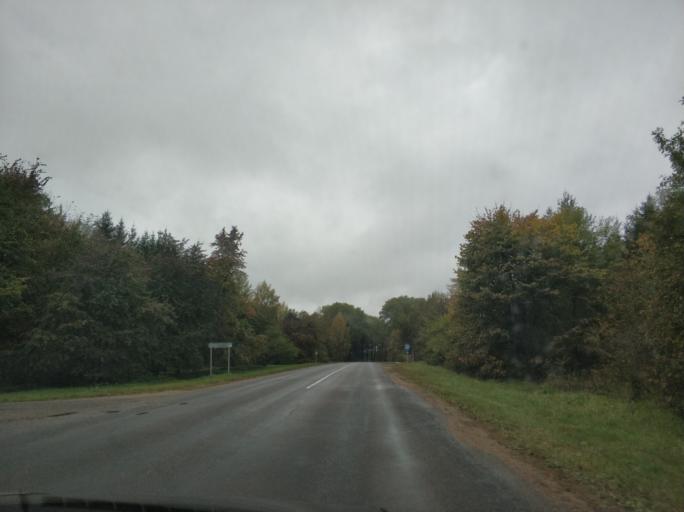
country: BY
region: Vitebsk
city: Polatsk
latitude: 55.4443
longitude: 28.9453
